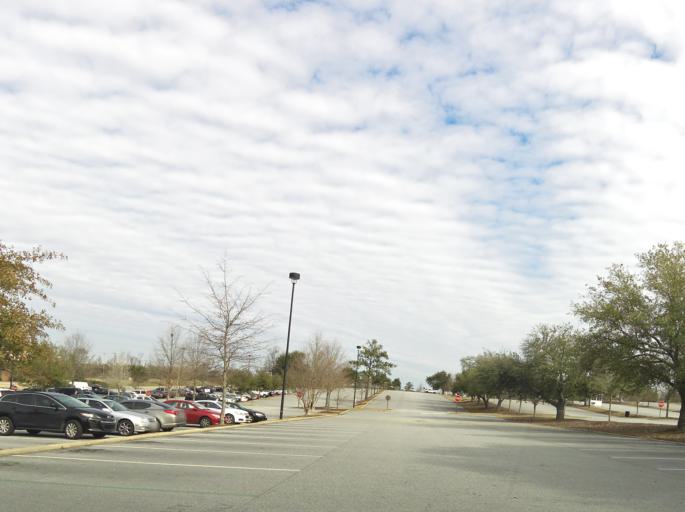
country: US
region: Georgia
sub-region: Bibb County
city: West Point
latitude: 32.8101
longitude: -83.7313
